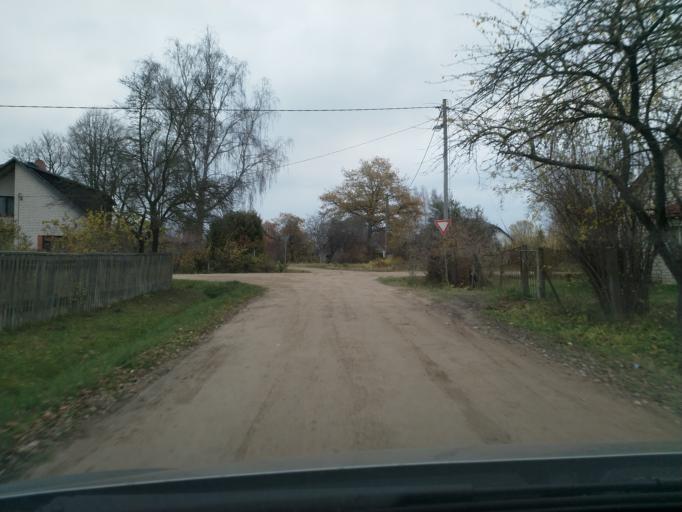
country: LV
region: Kuldigas Rajons
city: Kuldiga
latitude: 56.9613
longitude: 21.9950
